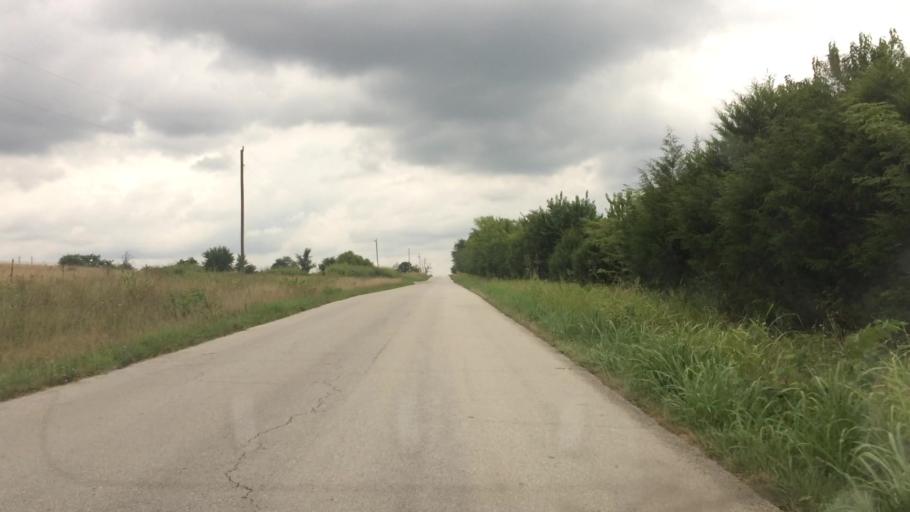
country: US
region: Missouri
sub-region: Greene County
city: Strafford
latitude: 37.3157
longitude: -93.0669
